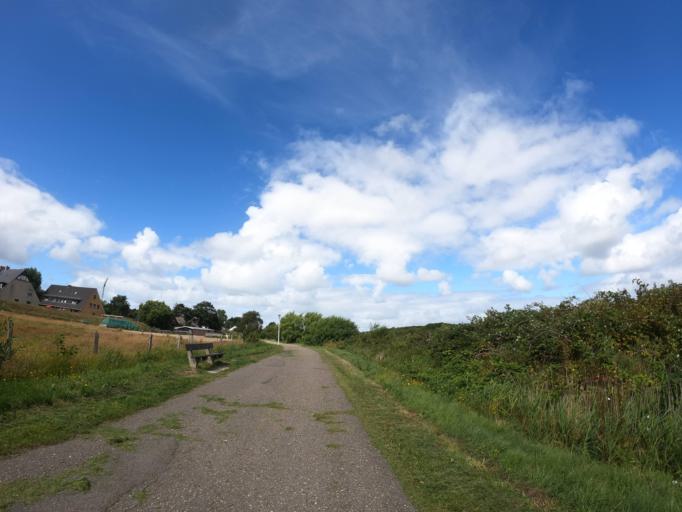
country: DE
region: Schleswig-Holstein
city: Westerland
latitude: 54.8957
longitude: 8.3143
